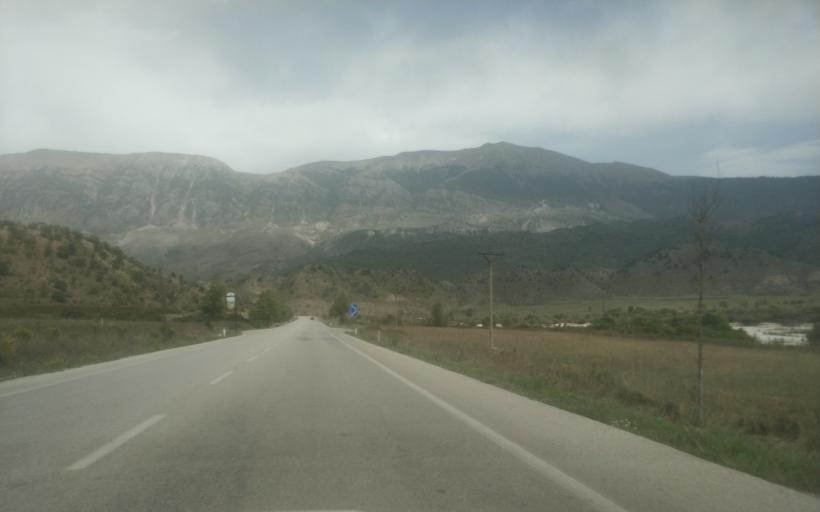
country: AL
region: Gjirokaster
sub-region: Rrethi i Gjirokastres
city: Picar
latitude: 40.1985
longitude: 20.0864
